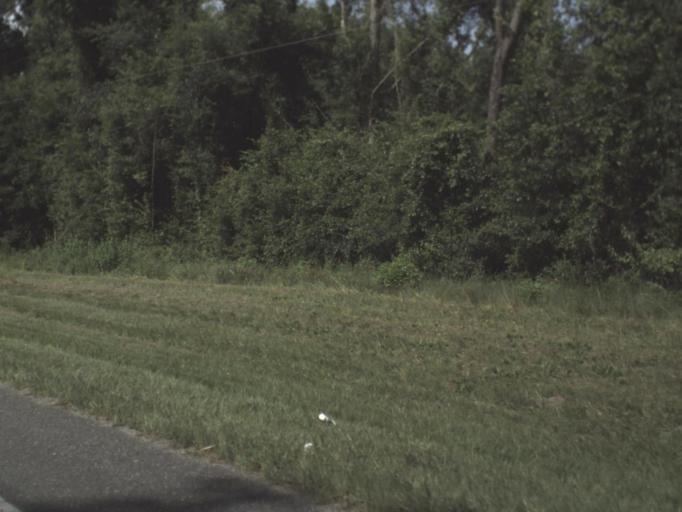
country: US
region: Florida
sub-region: Alachua County
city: High Springs
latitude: 29.9795
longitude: -82.7099
